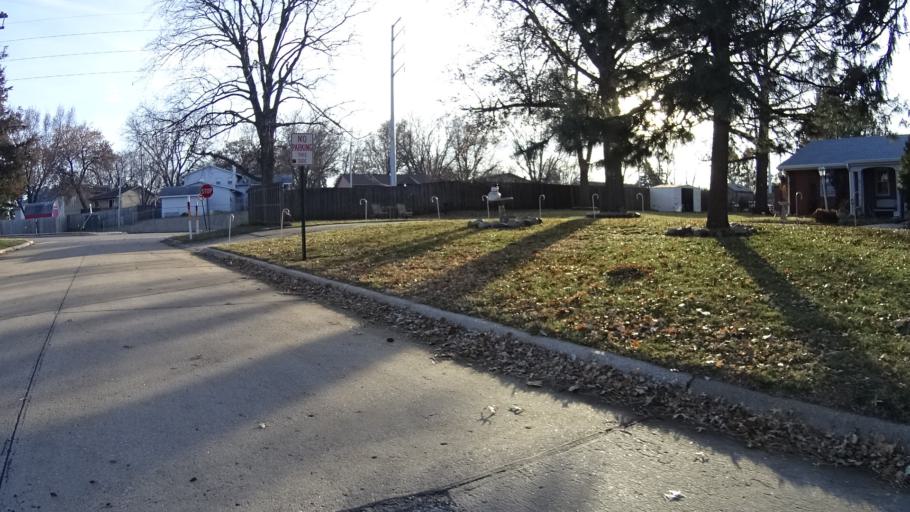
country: US
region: Nebraska
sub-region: Douglas County
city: Ralston
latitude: 41.1912
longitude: -96.0471
